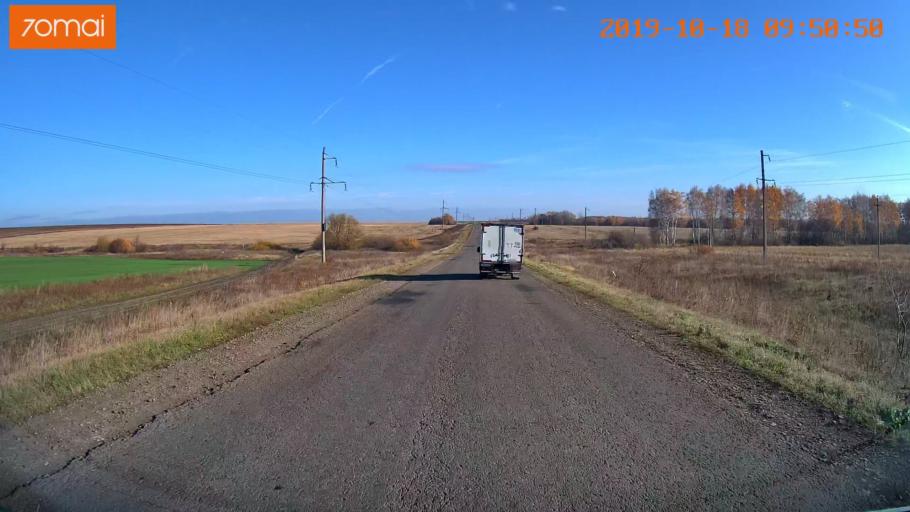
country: RU
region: Tula
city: Kazachka
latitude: 53.3334
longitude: 38.2832
